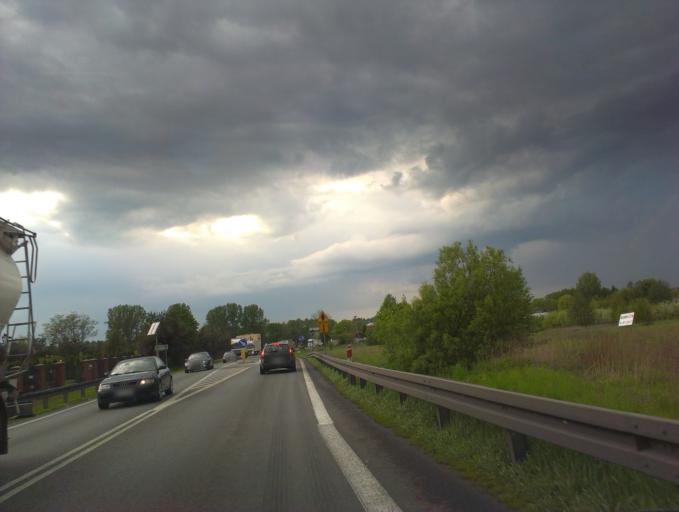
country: PL
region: Masovian Voivodeship
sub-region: Powiat grojecki
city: Pniewy
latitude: 51.8942
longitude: 20.7856
